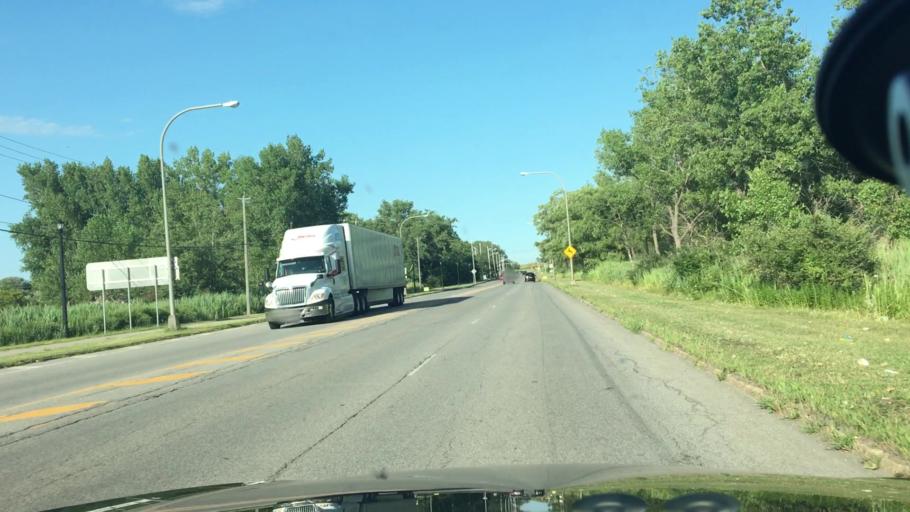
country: US
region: New York
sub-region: Erie County
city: Lackawanna
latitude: 42.8399
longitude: -78.8547
